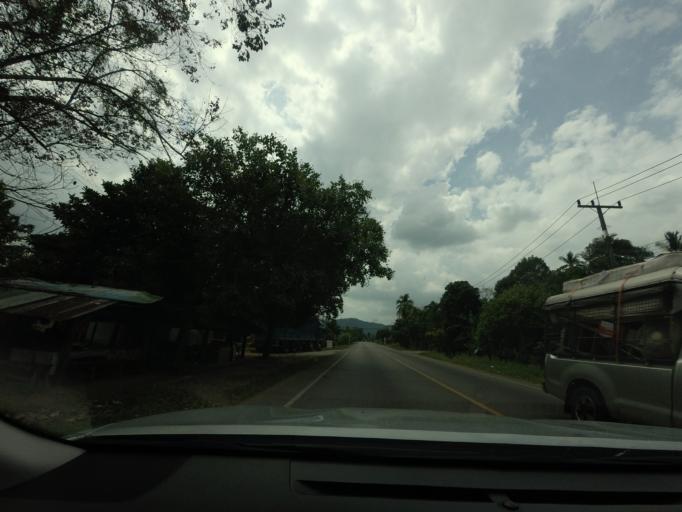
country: TH
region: Phangnga
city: Ban Ao Nang
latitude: 8.1240
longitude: 98.8047
